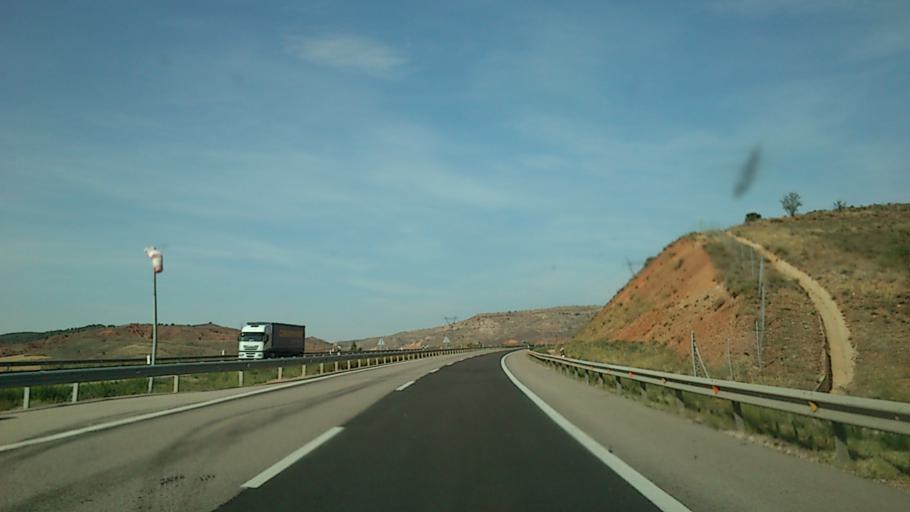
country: ES
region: Aragon
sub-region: Provincia de Teruel
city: Calamocha
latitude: 40.9497
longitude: -1.2725
